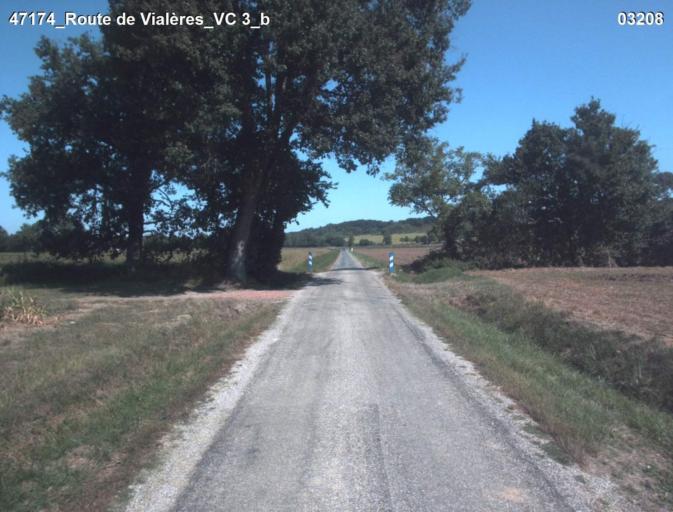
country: FR
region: Aquitaine
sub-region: Departement du Lot-et-Garonne
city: Nerac
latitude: 44.0606
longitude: 0.3850
